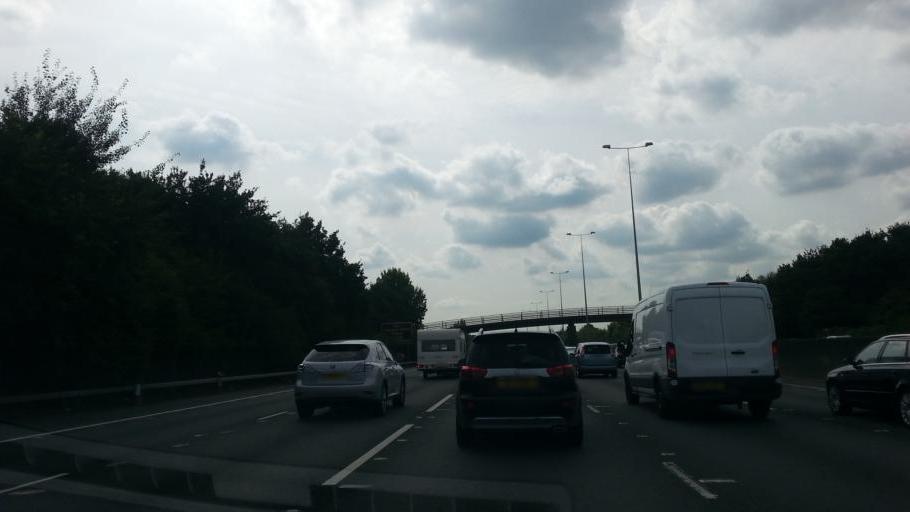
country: GB
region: England
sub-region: Surrey
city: Egham
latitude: 51.4153
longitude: -0.5400
